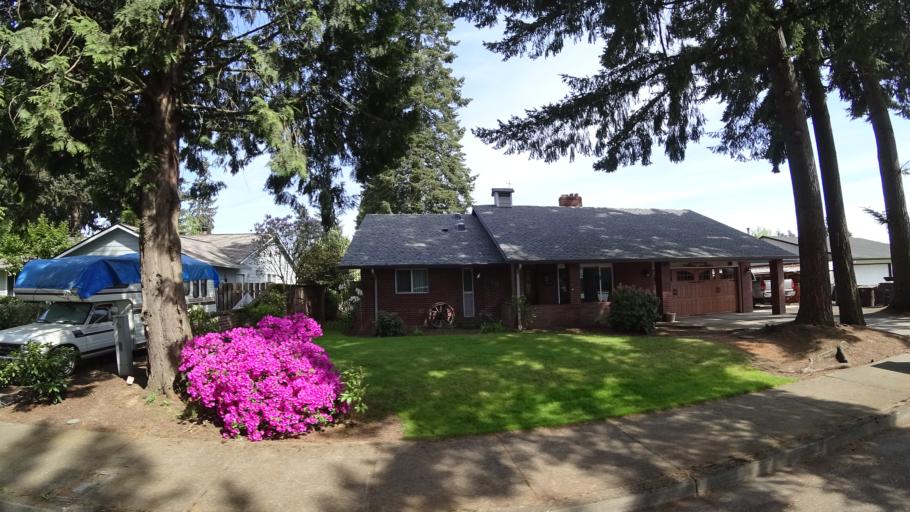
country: US
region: Oregon
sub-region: Washington County
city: Hillsboro
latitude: 45.5154
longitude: -122.9389
